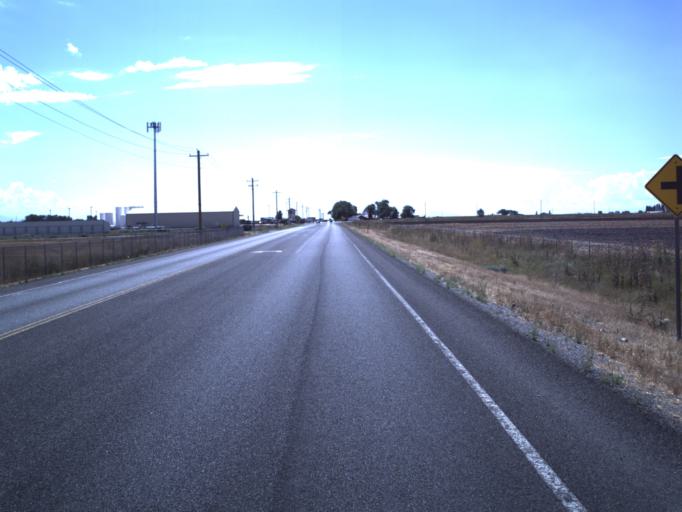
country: US
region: Utah
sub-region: Box Elder County
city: Honeyville
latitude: 41.5610
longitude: -112.1296
